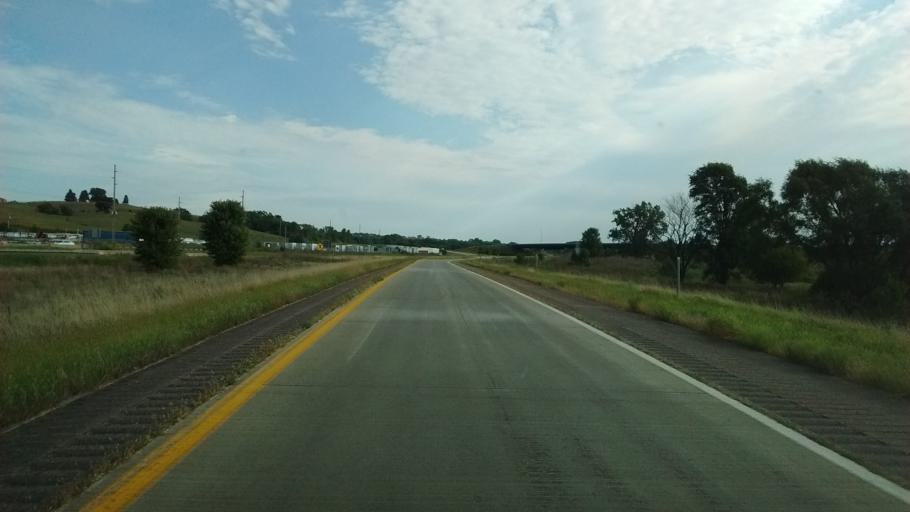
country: US
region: Iowa
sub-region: Woodbury County
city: Sioux City
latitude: 42.5487
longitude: -96.3477
